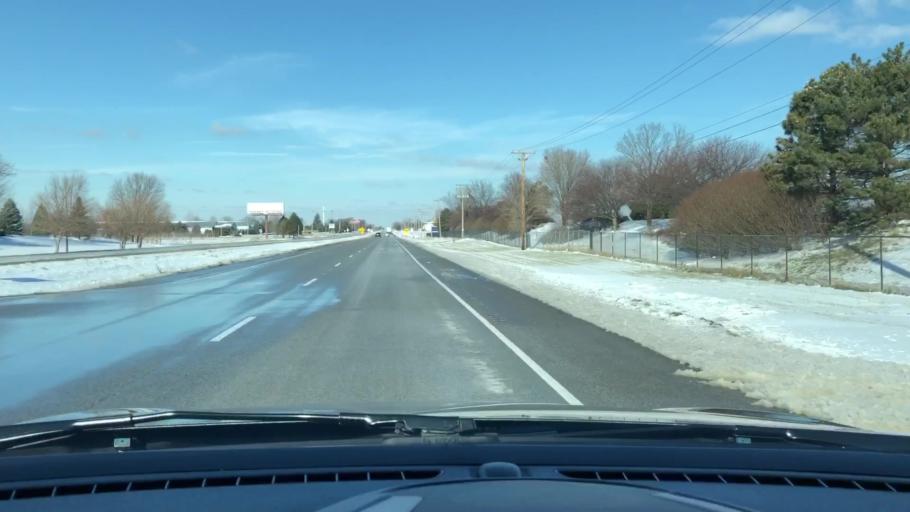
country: US
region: Illinois
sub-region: Will County
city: Preston Heights
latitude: 41.4627
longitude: -88.0794
